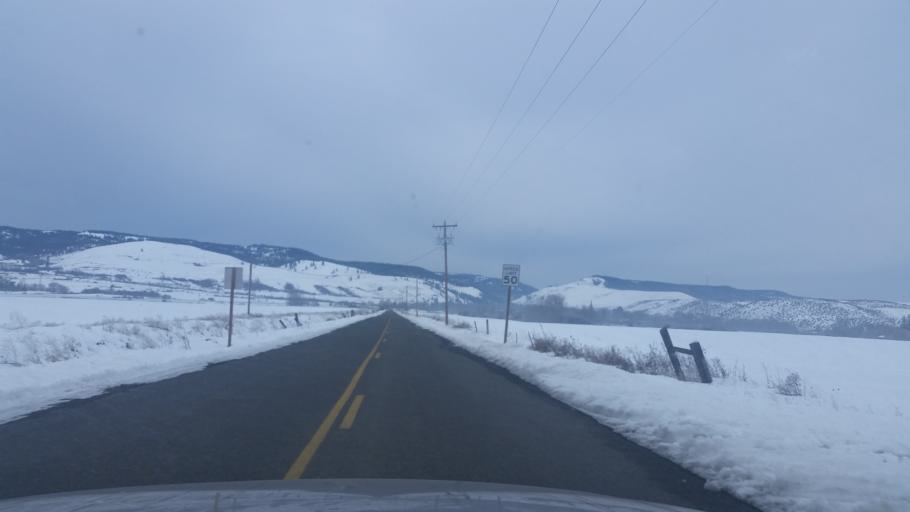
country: US
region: Washington
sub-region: Kittitas County
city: Ellensburg
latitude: 47.0799
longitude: -120.7088
